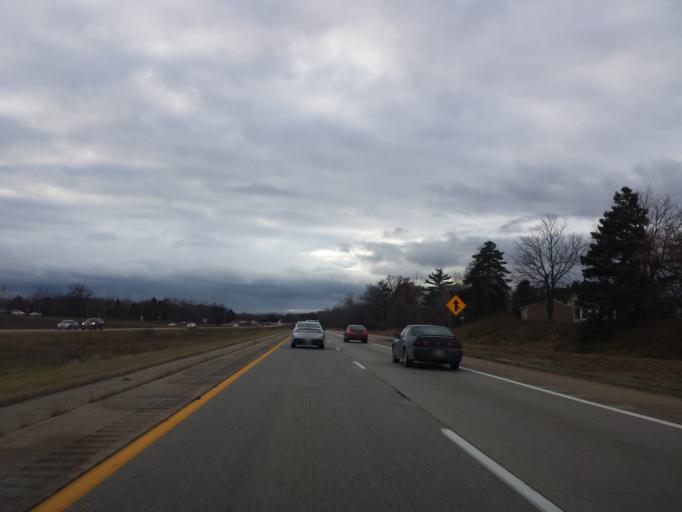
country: US
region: Michigan
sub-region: Ingham County
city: Haslett
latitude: 42.7993
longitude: -84.3520
